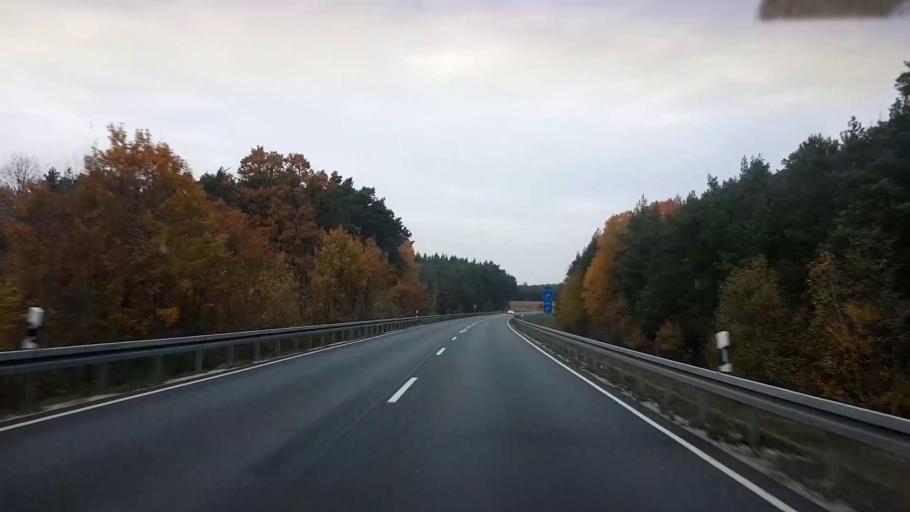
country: DE
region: Bavaria
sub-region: Upper Franconia
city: Pommersfelden
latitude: 49.7385
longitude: 10.8270
